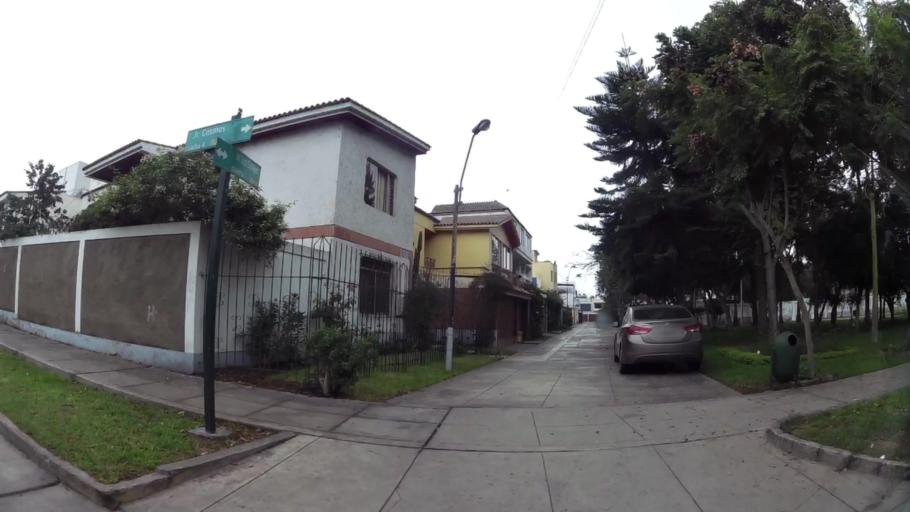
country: PE
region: Lima
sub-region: Lima
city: Surco
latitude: -12.1225
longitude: -76.9883
